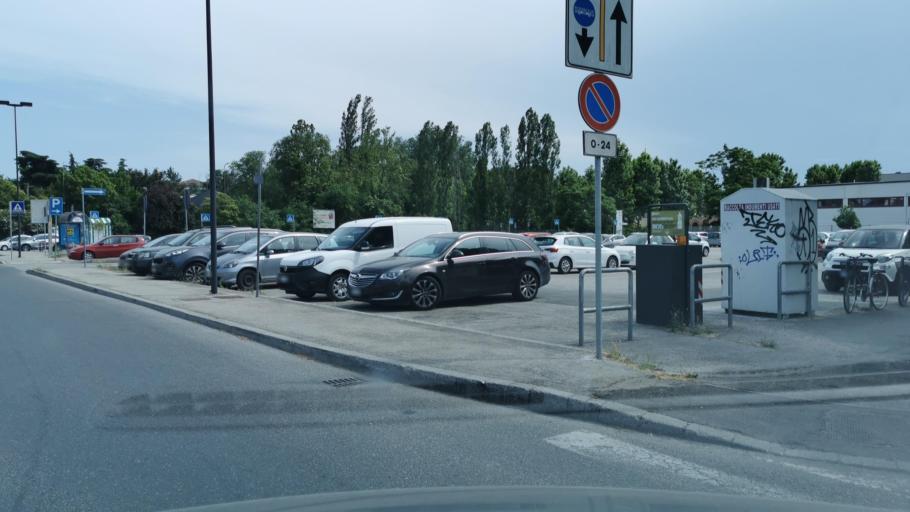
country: IT
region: Emilia-Romagna
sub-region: Provincia di Ravenna
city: Ravenna
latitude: 44.4141
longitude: 12.1864
